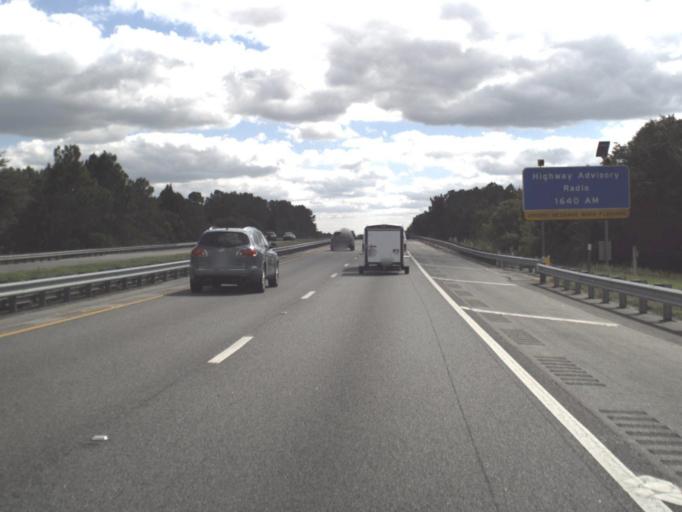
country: US
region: Florida
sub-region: Osceola County
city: Saint Cloud
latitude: 28.1533
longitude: -81.2981
